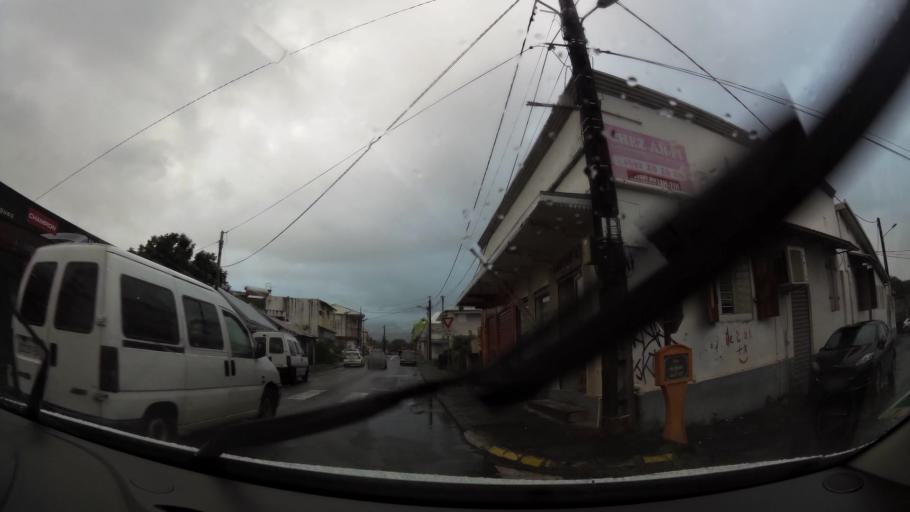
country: RE
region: Reunion
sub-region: Reunion
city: Saint-Benoit
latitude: -21.0358
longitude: 55.7163
